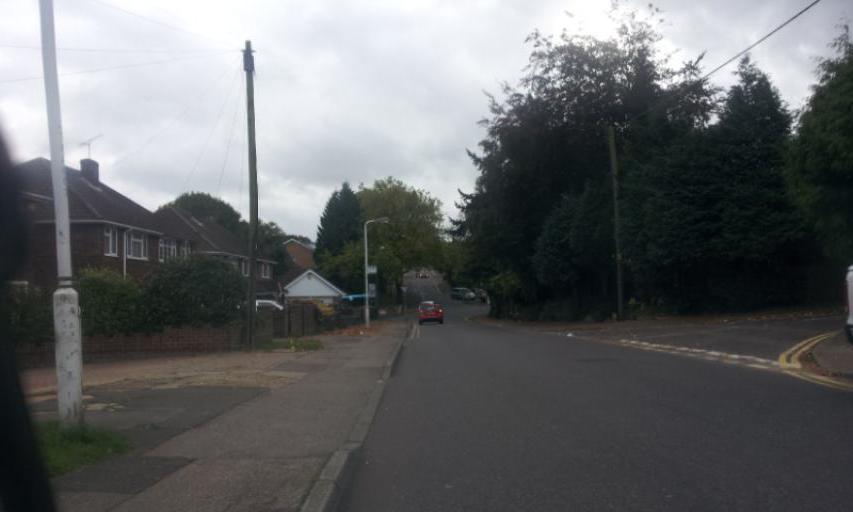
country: GB
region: England
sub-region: Kent
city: Boxley
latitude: 51.3368
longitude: 0.5214
